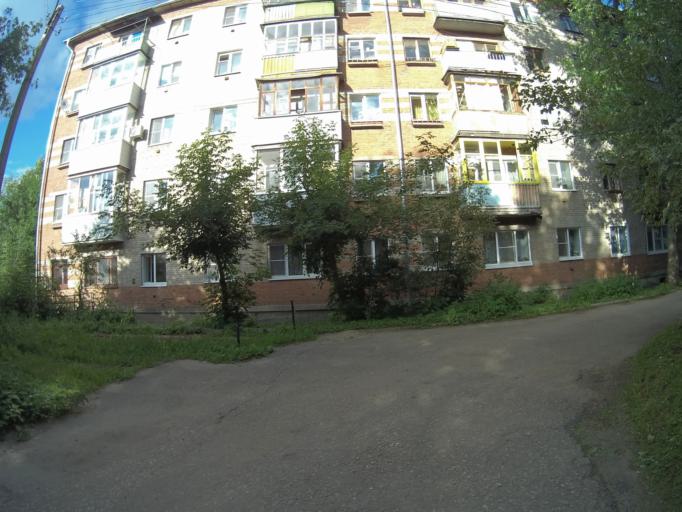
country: RU
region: Vladimir
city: Vladimir
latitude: 56.1480
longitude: 40.4284
